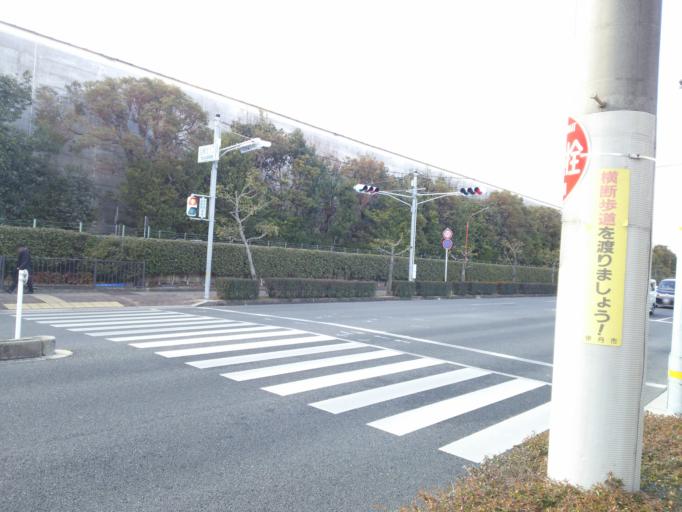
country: JP
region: Hyogo
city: Itami
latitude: 34.7845
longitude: 135.3954
